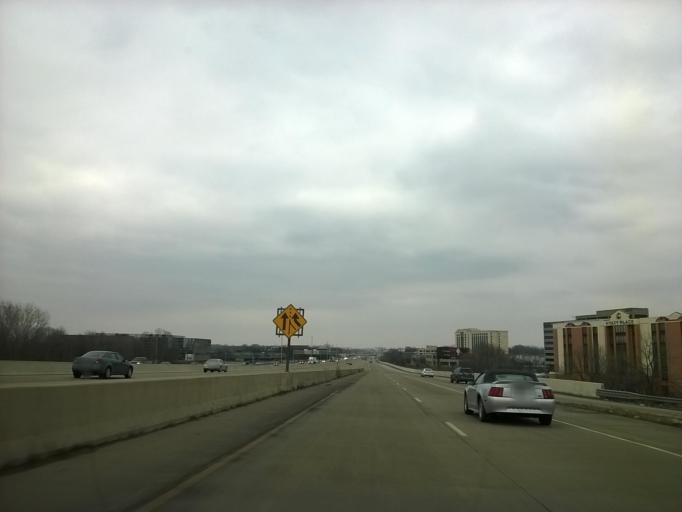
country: US
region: Indiana
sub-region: Marion County
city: Meridian Hills
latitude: 39.9208
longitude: -86.1110
